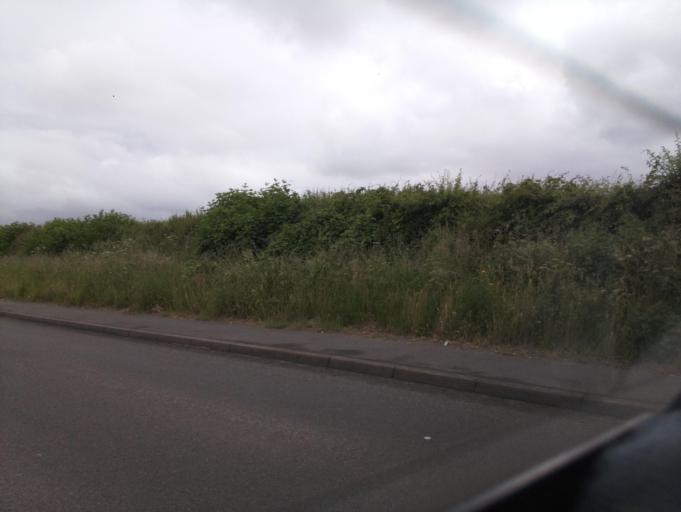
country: GB
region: England
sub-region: Staffordshire
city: Burton upon Trent
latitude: 52.8477
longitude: -1.6781
